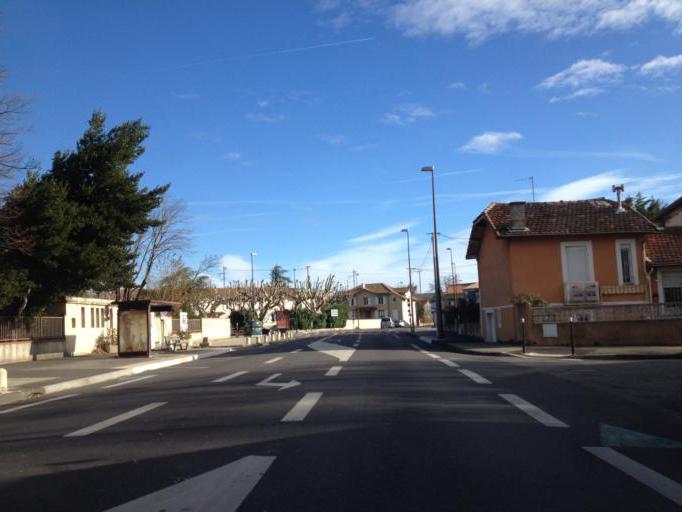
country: FR
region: Provence-Alpes-Cote d'Azur
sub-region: Departement du Vaucluse
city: Avignon
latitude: 43.9442
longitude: 4.8182
